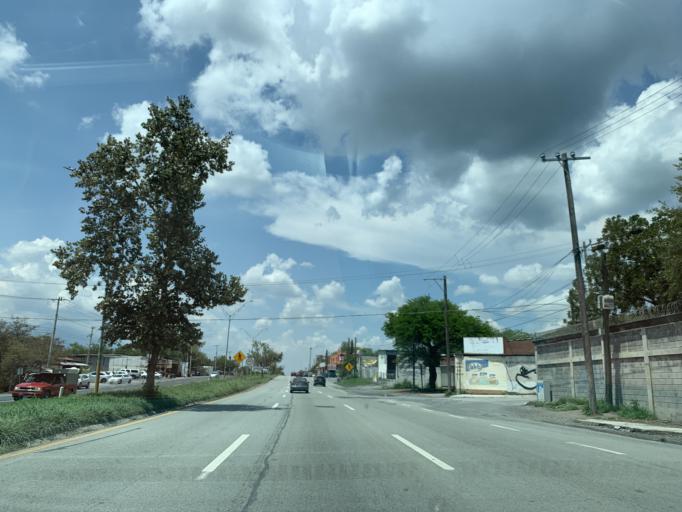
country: MX
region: Nuevo Leon
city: Santiago
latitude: 25.3818
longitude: -100.1133
